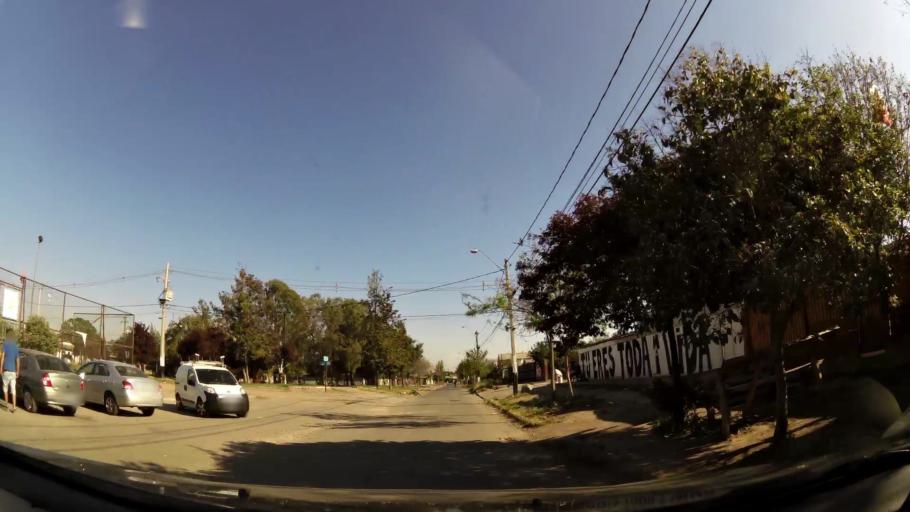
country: CL
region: Santiago Metropolitan
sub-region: Provincia de Santiago
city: La Pintana
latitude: -33.5762
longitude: -70.6521
